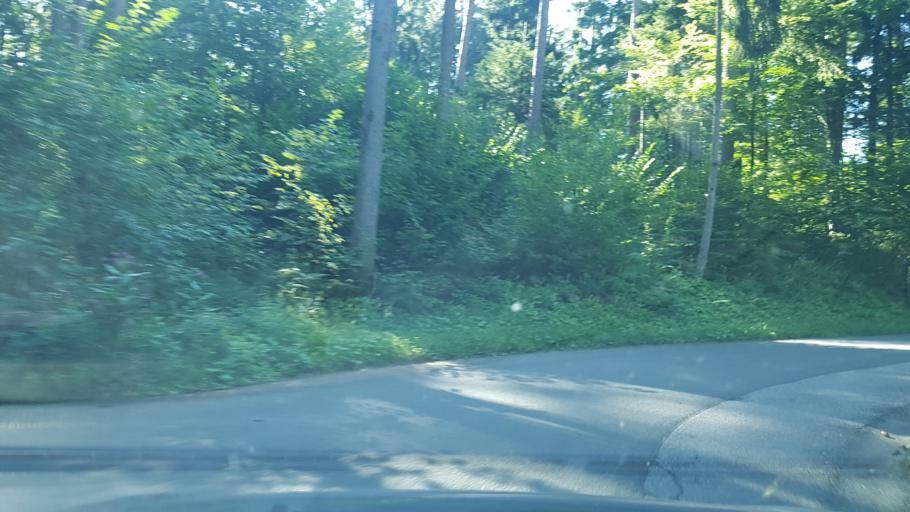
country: SI
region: Ravne na Koroskem
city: Kotlje
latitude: 46.5109
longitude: 14.9667
